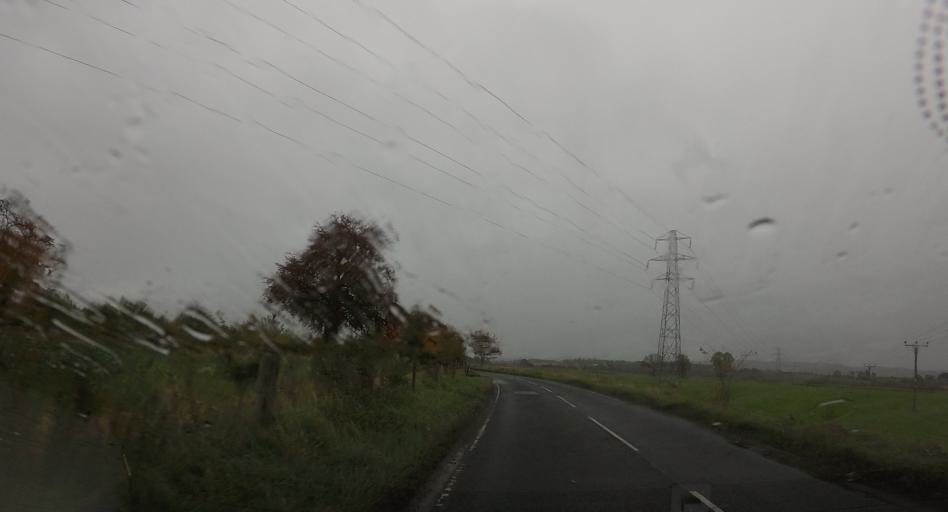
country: GB
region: Scotland
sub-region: Perth and Kinross
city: Coupar Angus
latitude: 56.5494
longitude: -3.3070
